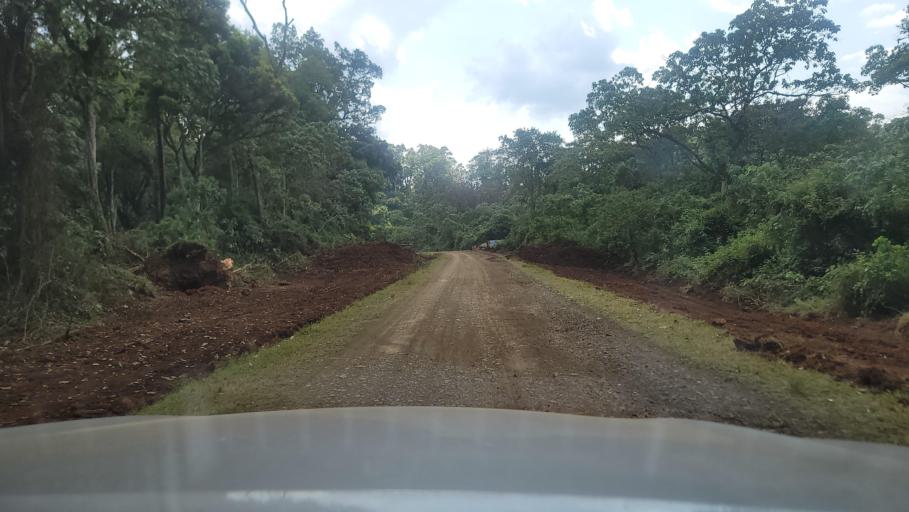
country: ET
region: Southern Nations, Nationalities, and People's Region
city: Bonga
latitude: 7.6602
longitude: 36.2472
